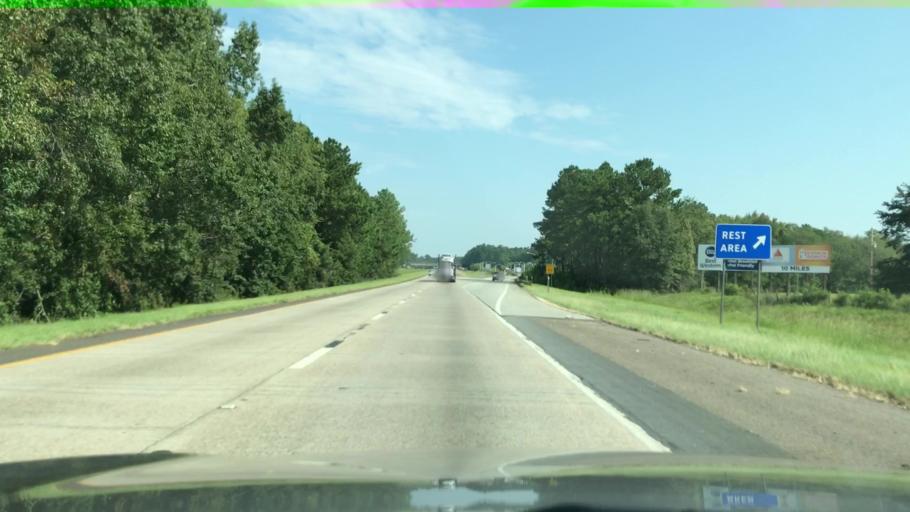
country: US
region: South Carolina
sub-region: Hampton County
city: Yemassee
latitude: 32.7962
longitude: -80.7735
